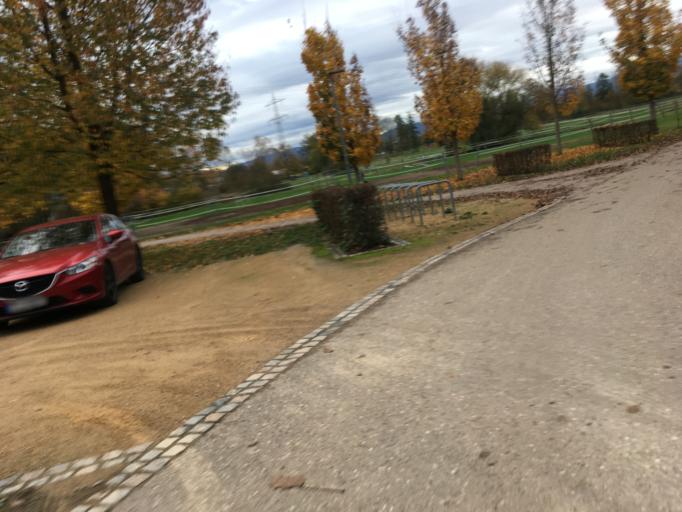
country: DE
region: Baden-Wuerttemberg
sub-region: Freiburg Region
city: Eichstetten
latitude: 48.0907
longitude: 7.7467
